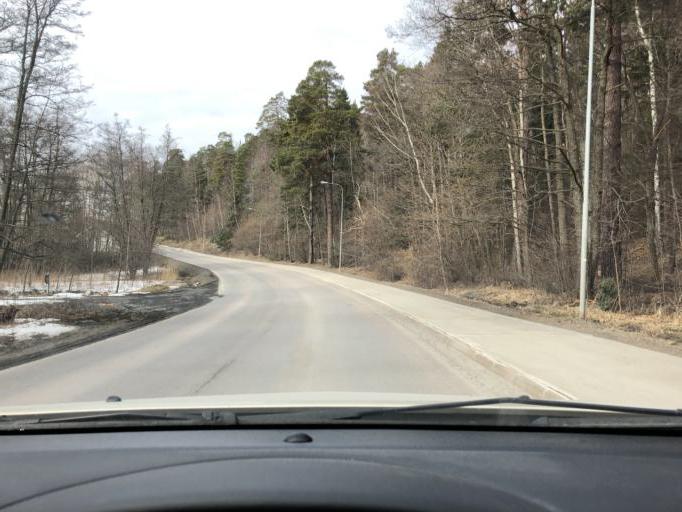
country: SE
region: Stockholm
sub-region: Nacka Kommun
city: Boo
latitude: 59.3331
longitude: 18.3085
